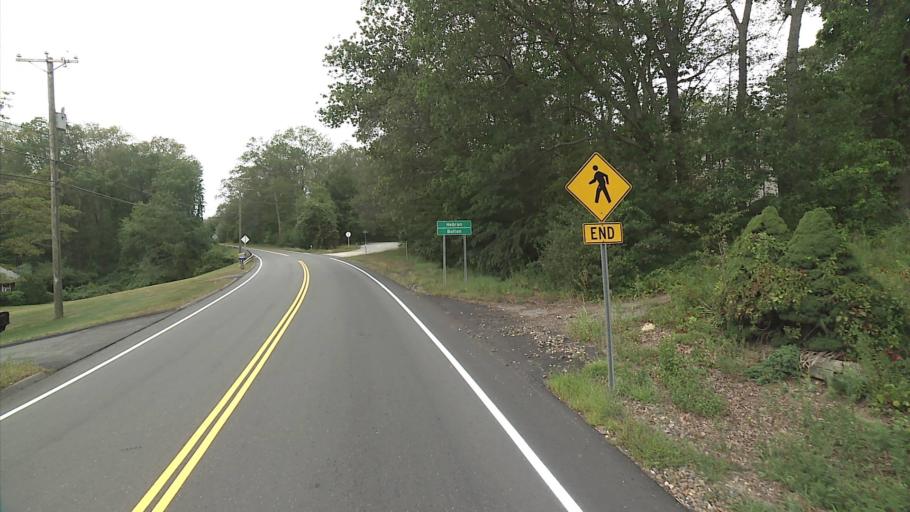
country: US
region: Connecticut
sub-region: Tolland County
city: Hebron
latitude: 41.6393
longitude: -72.3476
